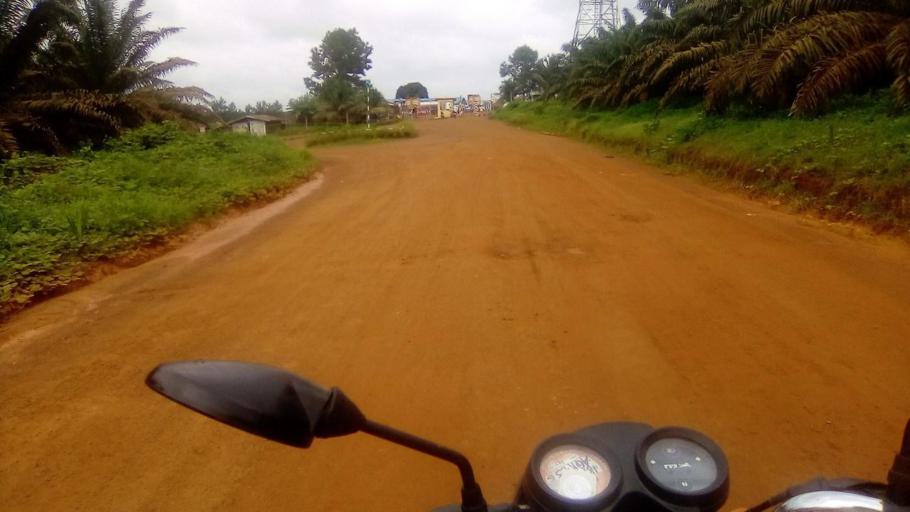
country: SL
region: Southern Province
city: Tongole
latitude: 7.4281
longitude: -11.8493
